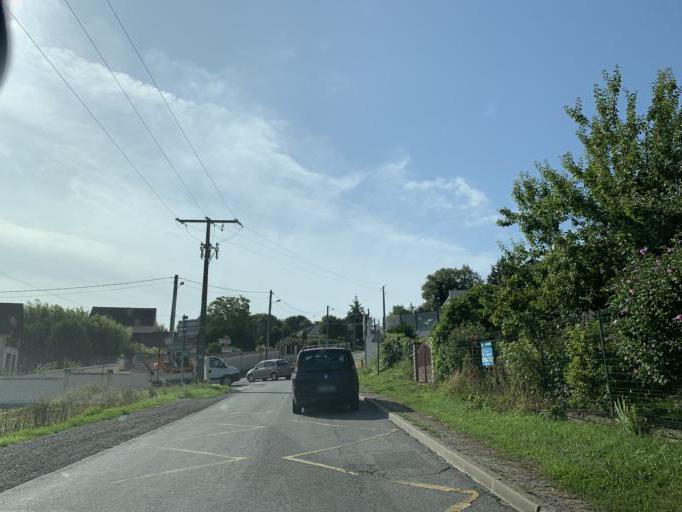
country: FR
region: Ile-de-France
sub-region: Departement de Seine-et-Marne
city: Chalifert
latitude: 48.8979
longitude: 2.7741
